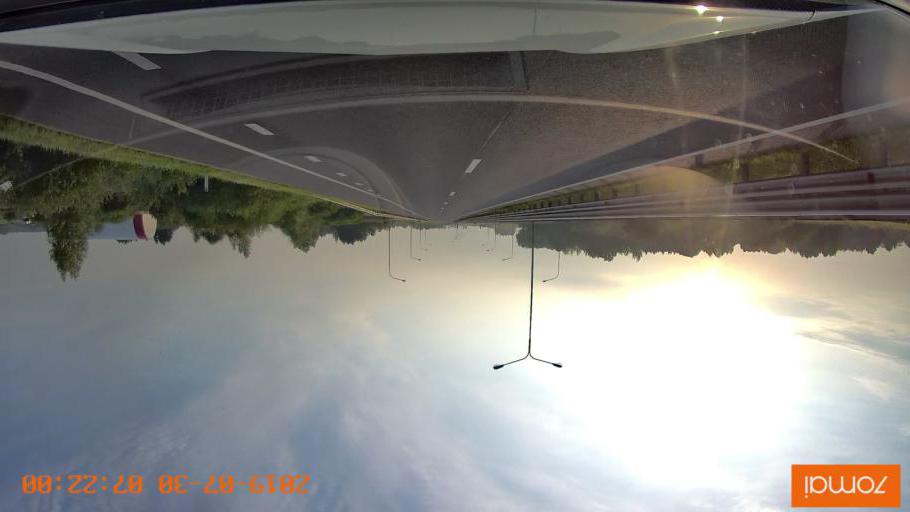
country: RU
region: Kaliningrad
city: Bol'shoe Isakovo
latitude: 54.6938
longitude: 20.7442
